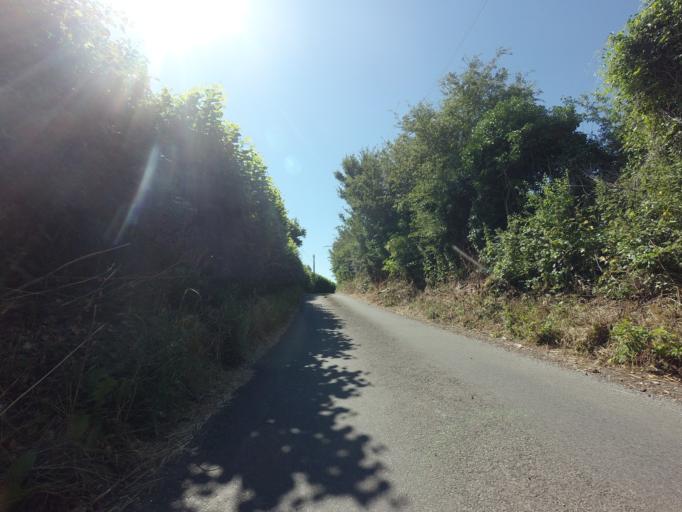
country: GB
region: England
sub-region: Kent
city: Swanley
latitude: 51.4084
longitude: 0.2053
